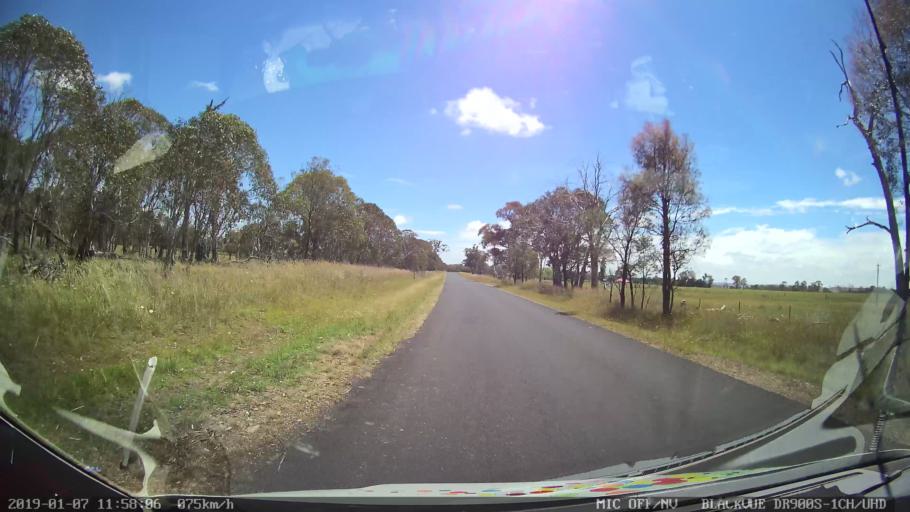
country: AU
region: New South Wales
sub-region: Guyra
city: Guyra
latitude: -30.2571
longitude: 151.6674
